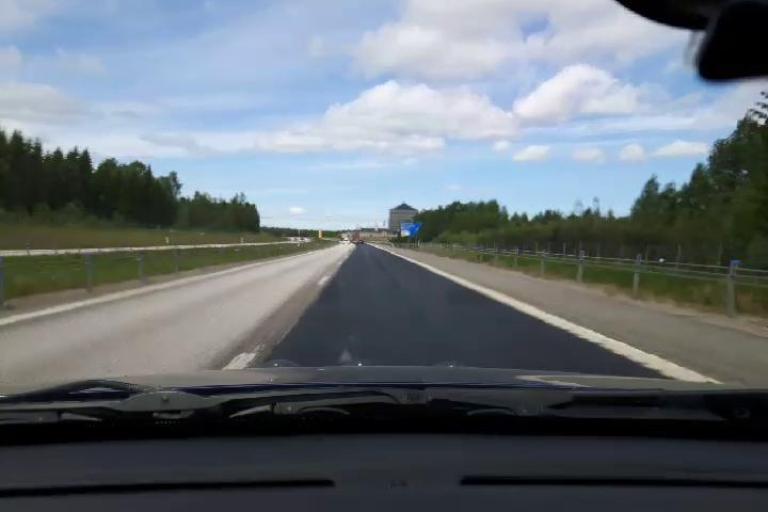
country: SE
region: Uppsala
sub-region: Alvkarleby Kommun
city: AElvkarleby
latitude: 60.4565
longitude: 17.4152
